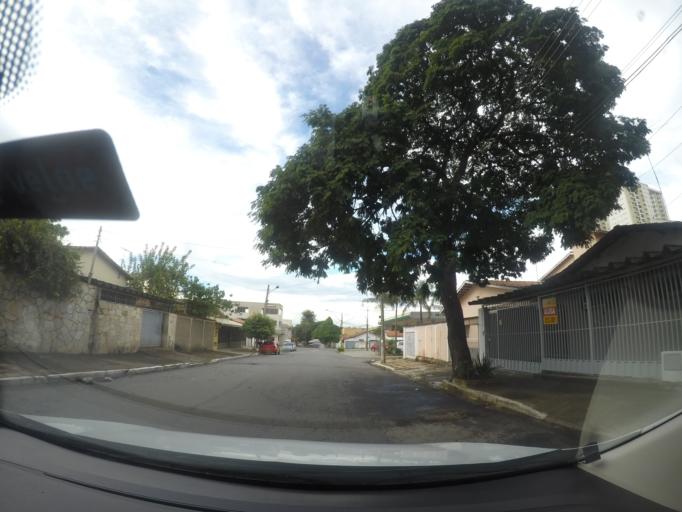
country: BR
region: Goias
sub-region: Goiania
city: Goiania
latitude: -16.6657
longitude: -49.2923
